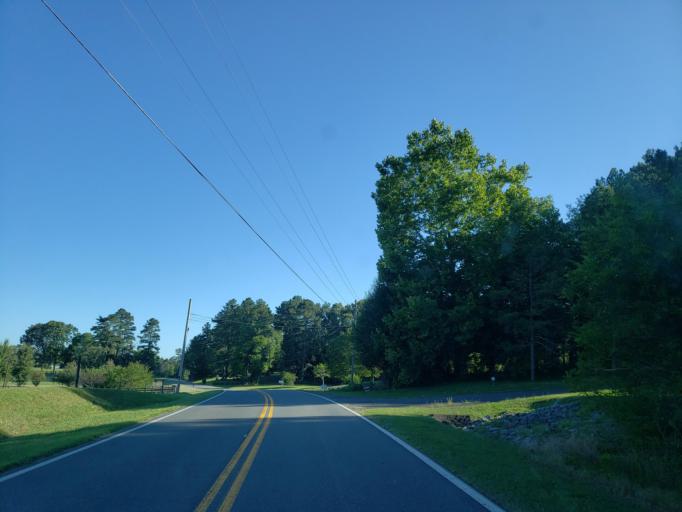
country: US
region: Georgia
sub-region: Floyd County
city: Shannon
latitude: 34.3700
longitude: -85.1323
